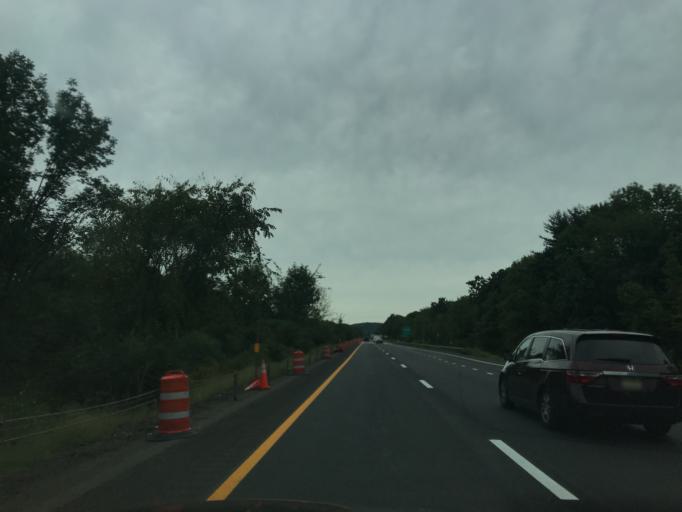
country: US
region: Pennsylvania
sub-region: Susquehanna County
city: Hallstead
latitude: 42.0238
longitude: -75.7844
